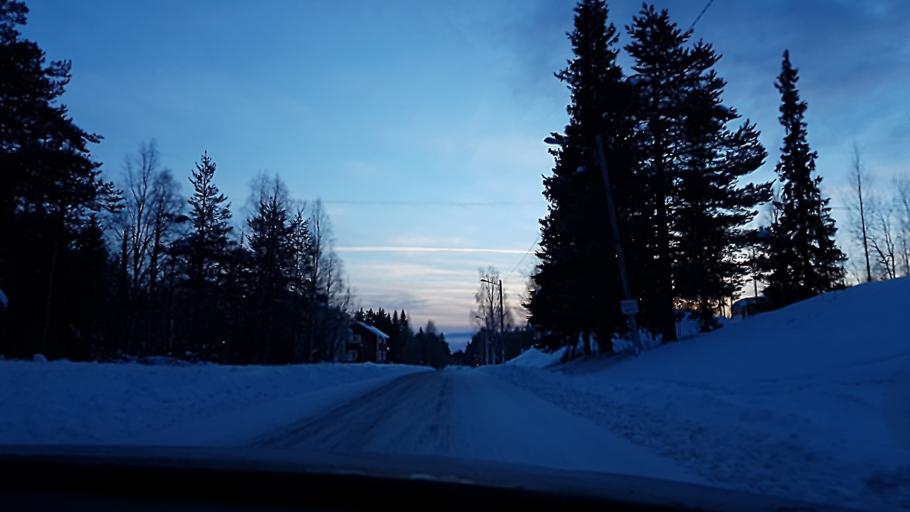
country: SE
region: Norrbotten
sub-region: Jokkmokks Kommun
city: Jokkmokk
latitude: 66.1480
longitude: 19.9879
